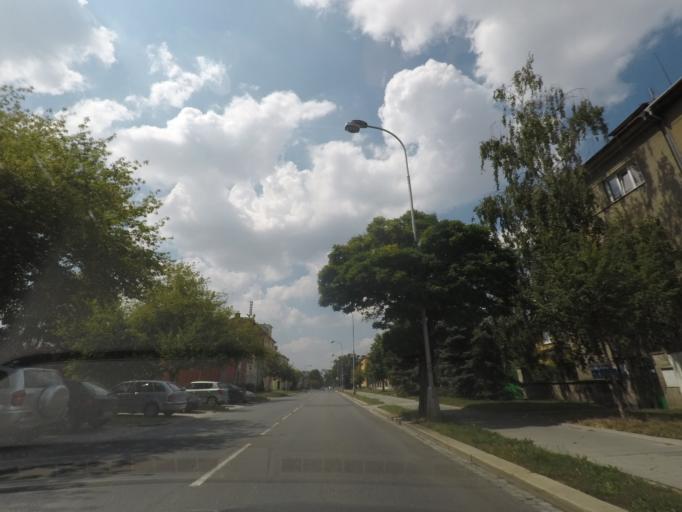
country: CZ
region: Olomoucky
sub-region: Okres Olomouc
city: Olomouc
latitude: 49.5852
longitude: 17.2509
